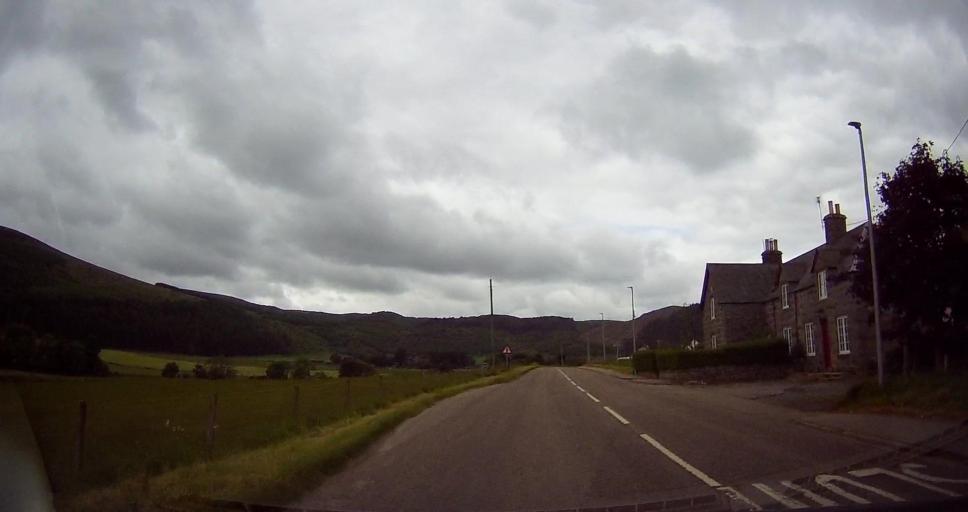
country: GB
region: Scotland
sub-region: Highland
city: Dornoch
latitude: 57.9903
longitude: -4.1596
